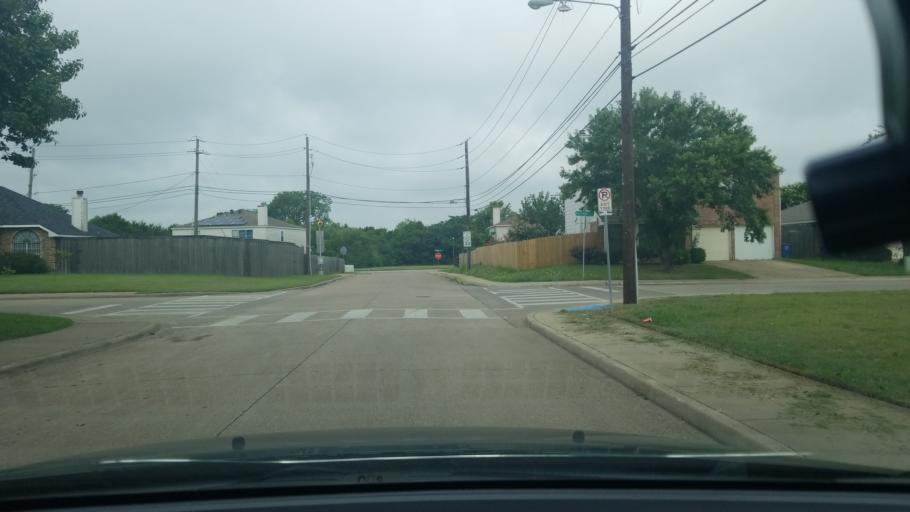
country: US
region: Texas
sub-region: Dallas County
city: Balch Springs
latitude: 32.7841
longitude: -96.6933
